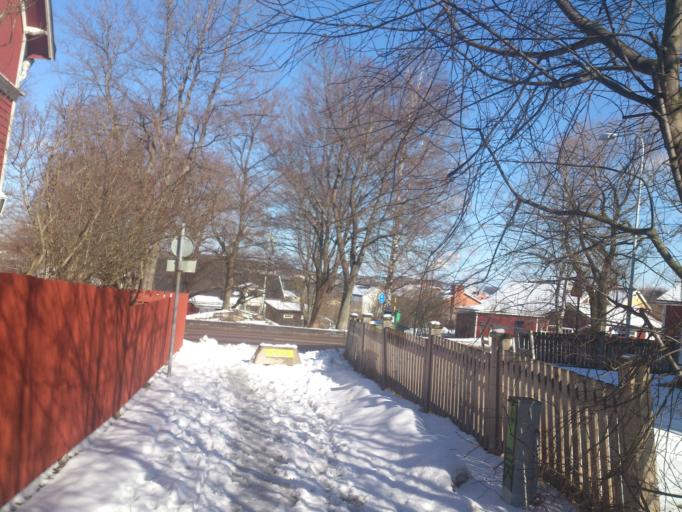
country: SE
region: Vaesternorrland
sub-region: Sundsvalls Kommun
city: Sundsvall
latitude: 62.3800
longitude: 17.3330
